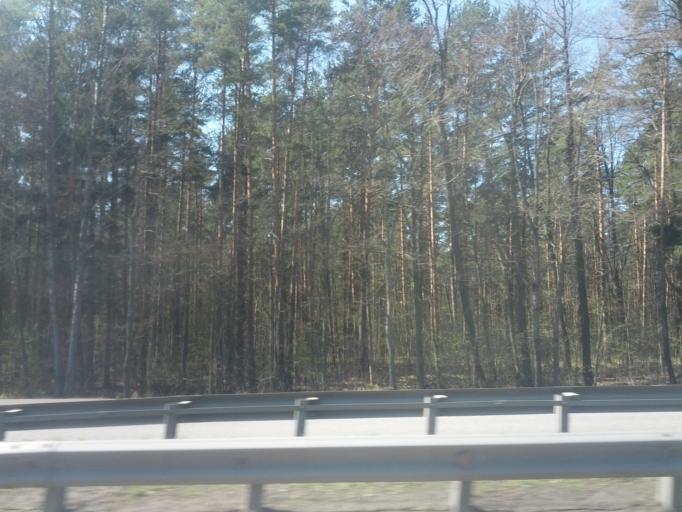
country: RU
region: St.-Petersburg
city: Tarkhovka
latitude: 60.0695
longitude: 29.9700
